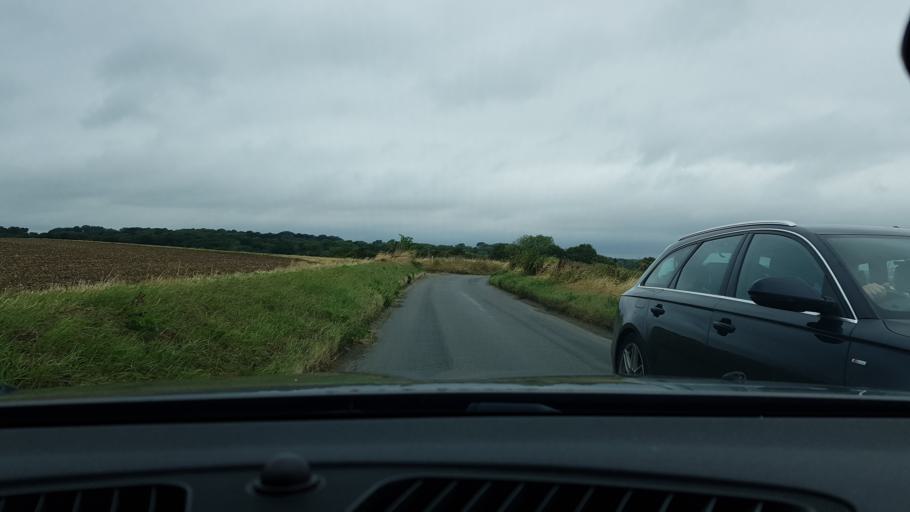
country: GB
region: England
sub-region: Wiltshire
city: Shalbourne
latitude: 51.3754
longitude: -1.5350
